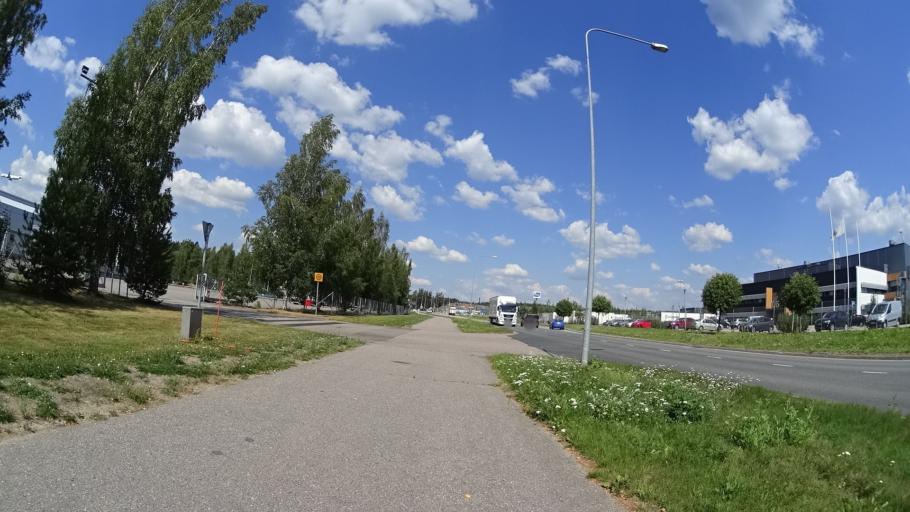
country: FI
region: Uusimaa
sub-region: Helsinki
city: Vantaa
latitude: 60.3415
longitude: 25.0220
